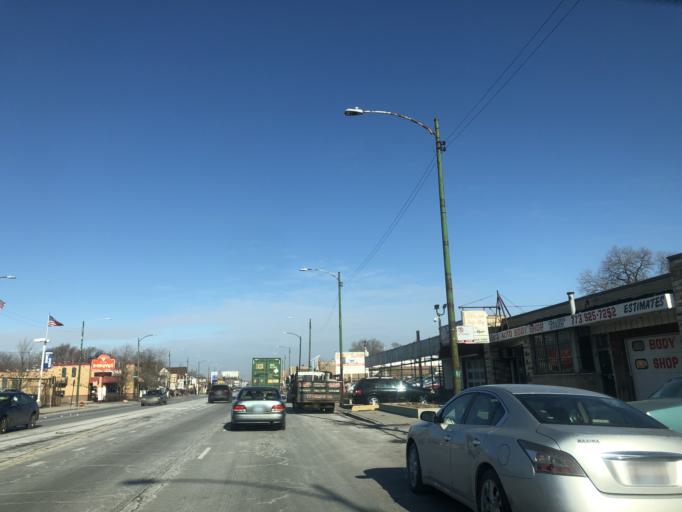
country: US
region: Illinois
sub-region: Cook County
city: Evergreen Park
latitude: 41.7603
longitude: -87.6831
